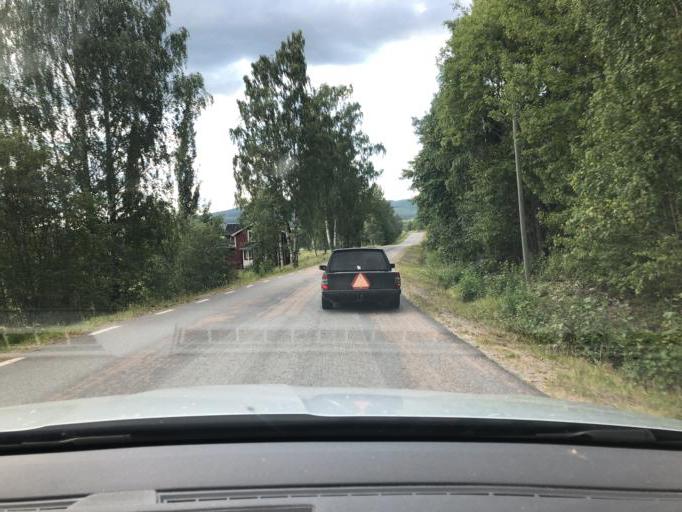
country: SE
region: Vaesternorrland
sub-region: Solleftea Kommun
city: Solleftea
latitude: 63.2043
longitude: 17.1449
